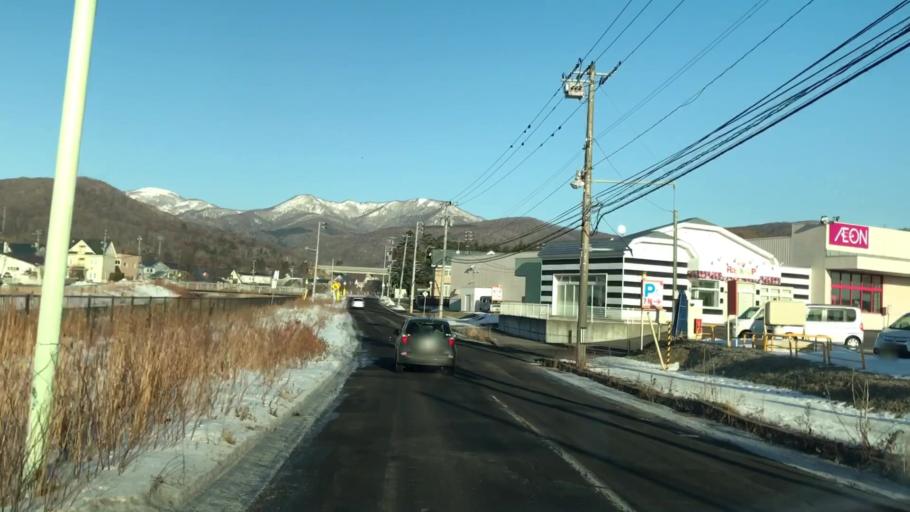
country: JP
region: Hokkaido
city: Muroran
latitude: 42.3852
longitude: 141.0712
